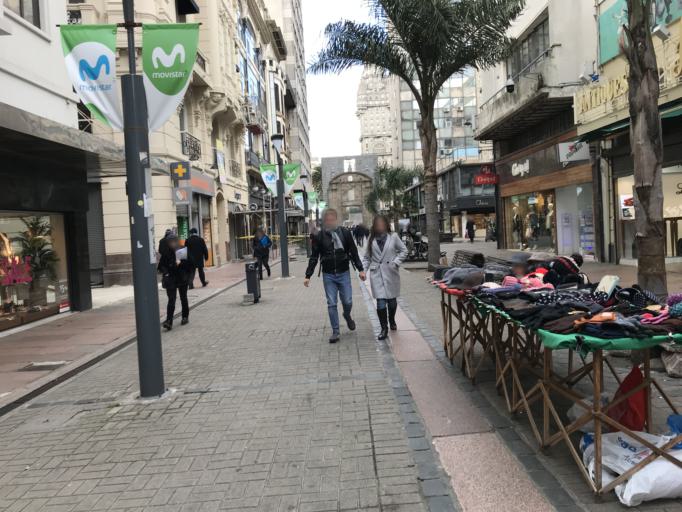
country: UY
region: Montevideo
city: Montevideo
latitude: -34.9065
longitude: -56.2020
